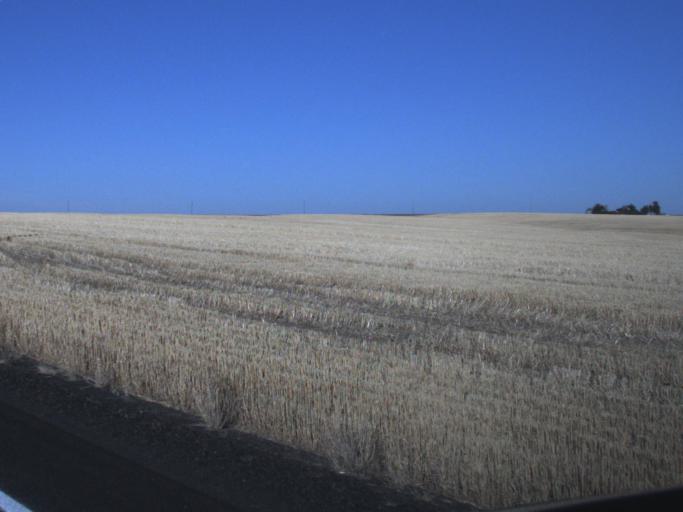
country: US
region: Washington
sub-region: Adams County
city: Ritzville
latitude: 46.9231
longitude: -118.3434
